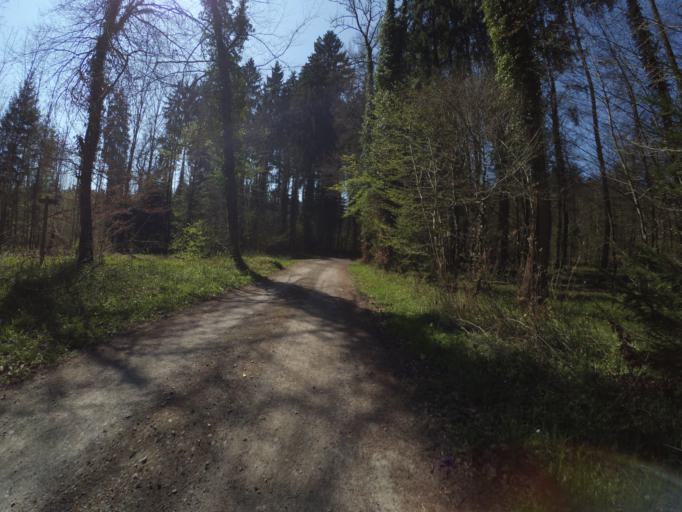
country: CH
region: Thurgau
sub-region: Frauenfeld District
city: Diessenhofen
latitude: 47.6428
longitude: 8.7432
